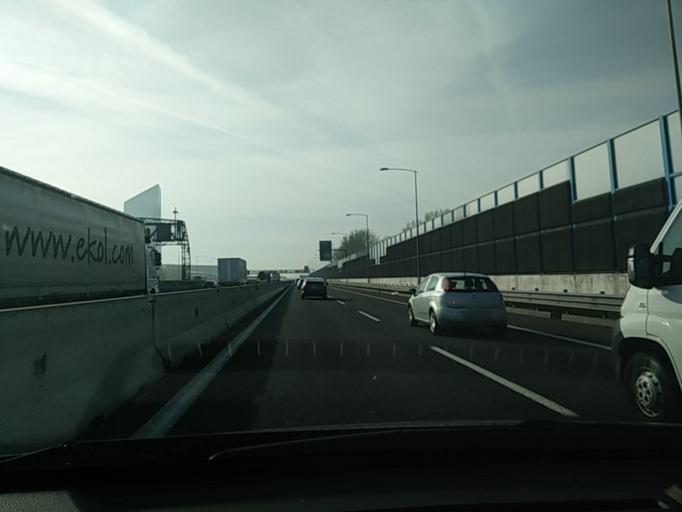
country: IT
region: Emilia-Romagna
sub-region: Provincia di Bologna
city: San Lazzaro
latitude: 44.5004
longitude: 11.3848
